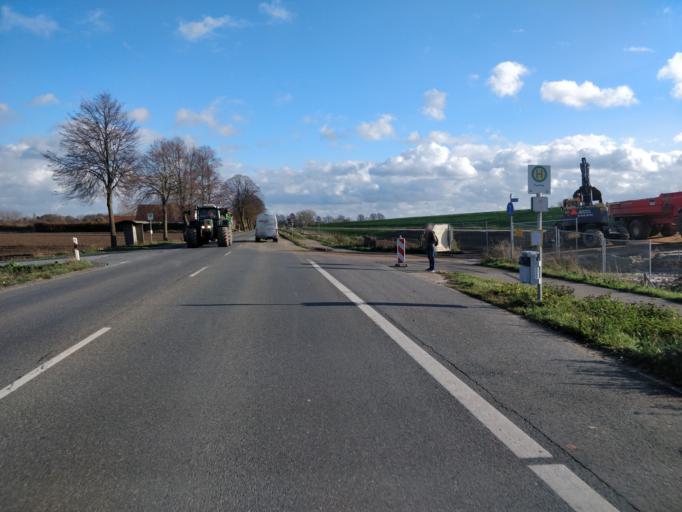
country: NL
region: Gelderland
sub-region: Oude IJsselstreek
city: Gendringen
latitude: 51.8158
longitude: 6.3557
